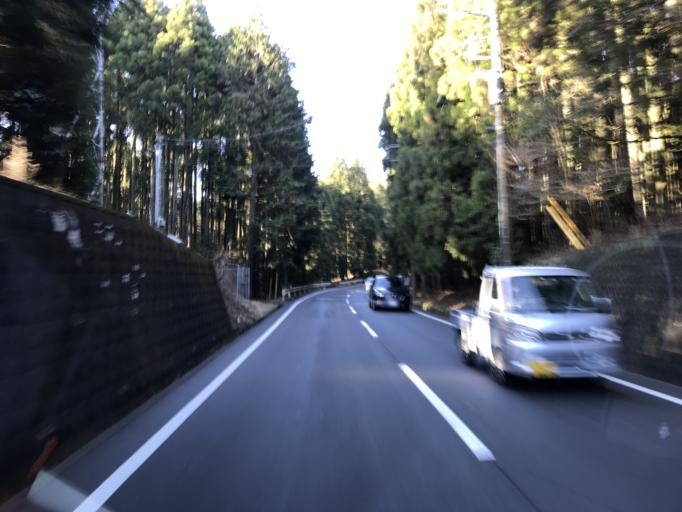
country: JP
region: Shizuoka
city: Gotemba
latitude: 35.2603
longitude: 138.8280
